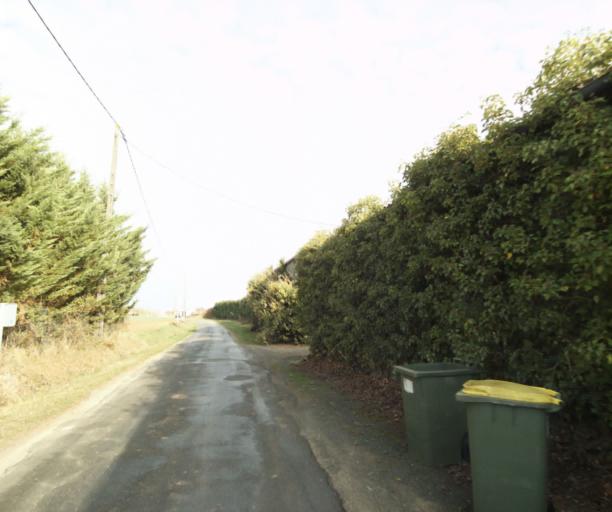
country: FR
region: Poitou-Charentes
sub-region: Departement de la Charente-Maritime
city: Corme-Royal
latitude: 45.7263
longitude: -0.7870
